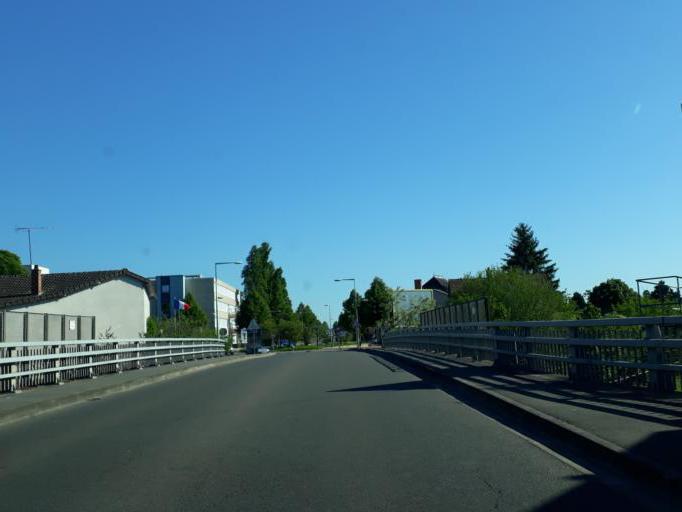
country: FR
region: Bourgogne
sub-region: Departement de la Nievre
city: Cosne-Cours-sur-Loire
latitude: 47.4046
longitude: 2.9225
